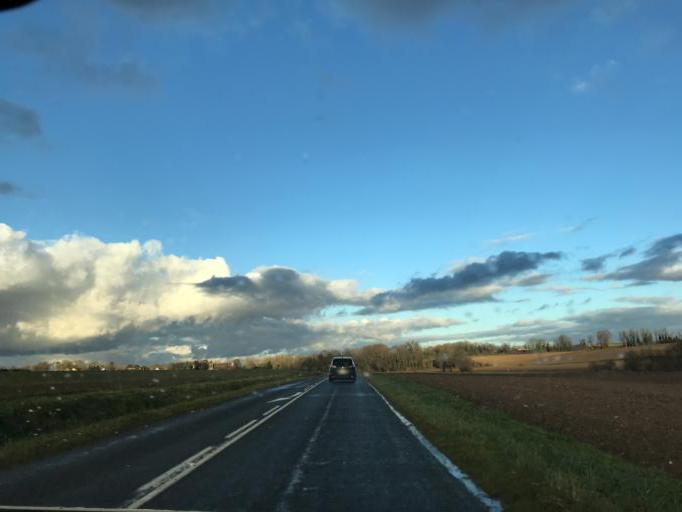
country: FR
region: Ile-de-France
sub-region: Departement de Seine-et-Marne
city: Juilly
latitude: 48.9934
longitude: 2.6979
